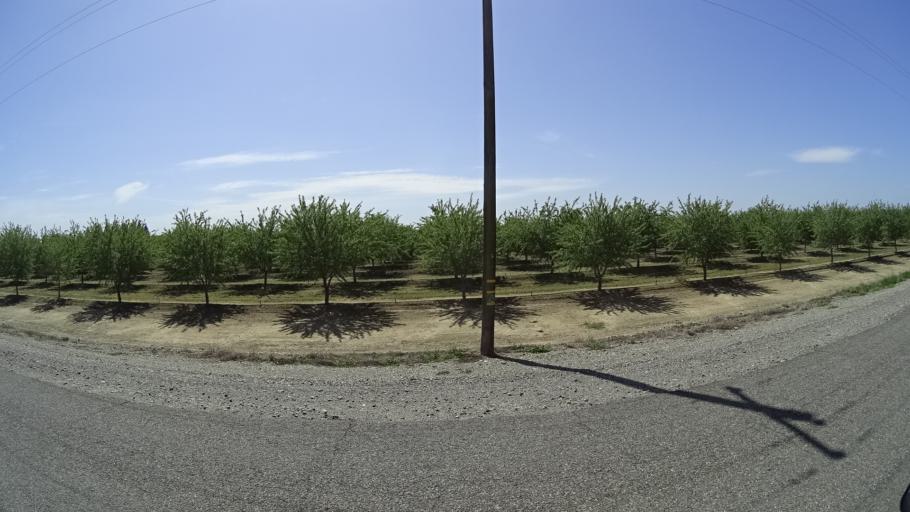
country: US
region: California
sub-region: Glenn County
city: Hamilton City
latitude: 39.6524
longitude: -122.0776
